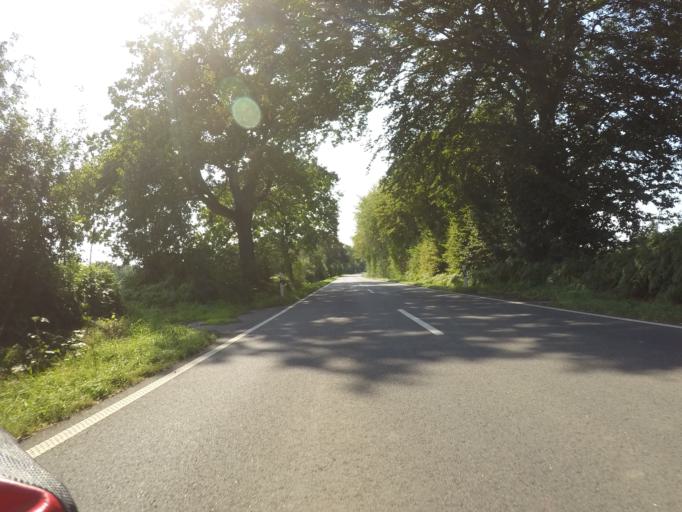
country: DE
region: Schleswig-Holstein
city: Huttblek
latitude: 53.8416
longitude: 10.0571
